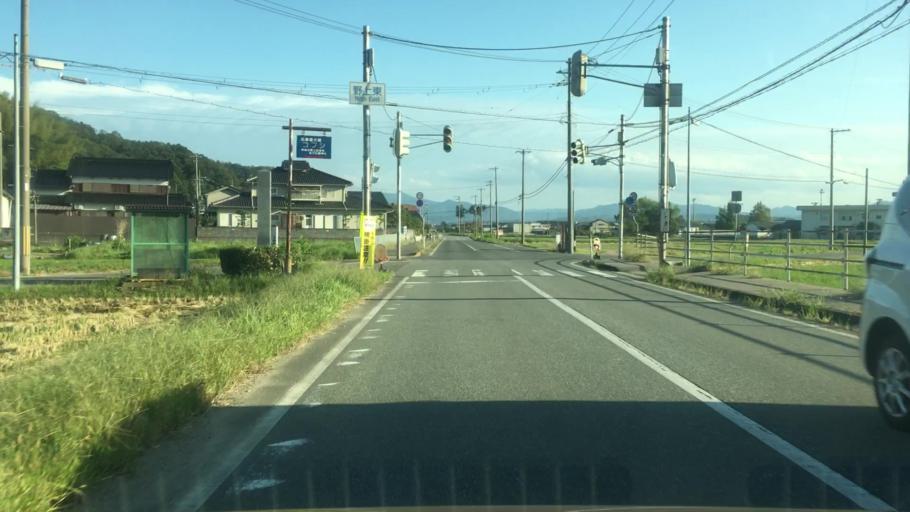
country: JP
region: Hyogo
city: Toyooka
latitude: 35.5654
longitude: 134.8199
